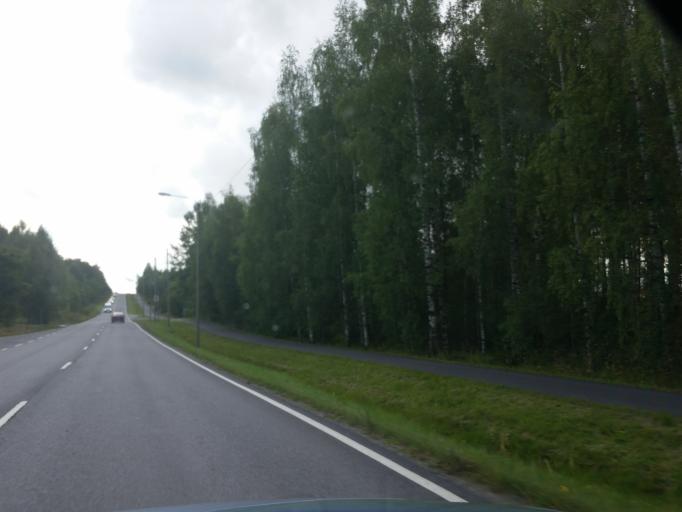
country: FI
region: Varsinais-Suomi
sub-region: Aboland-Turunmaa
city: Laensi-Turunmaa
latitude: 60.2946
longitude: 22.2682
